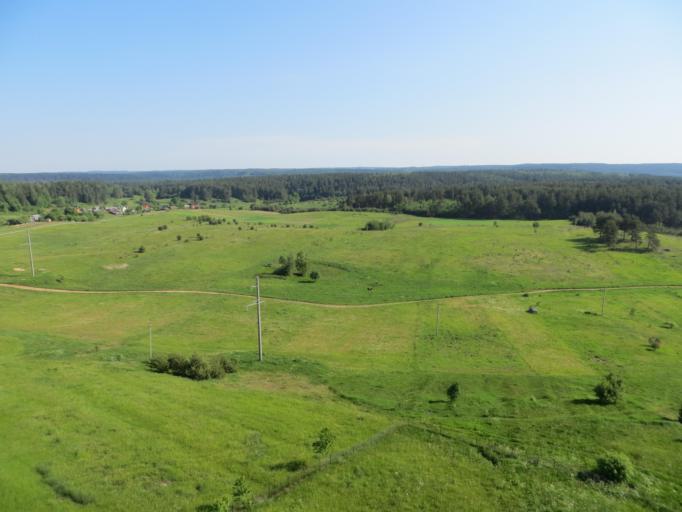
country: LT
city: Lentvaris
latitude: 54.7156
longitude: 24.9911
